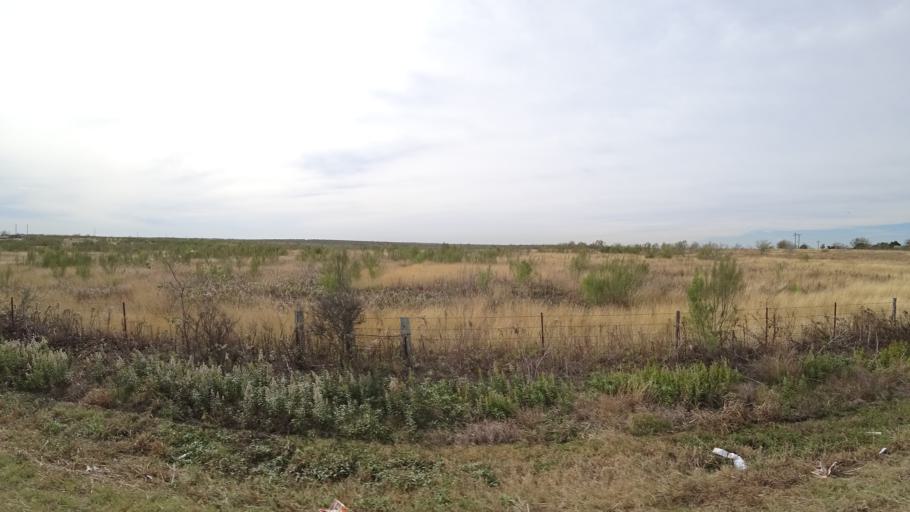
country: US
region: Texas
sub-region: Travis County
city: Garfield
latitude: 30.1263
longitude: -97.6003
